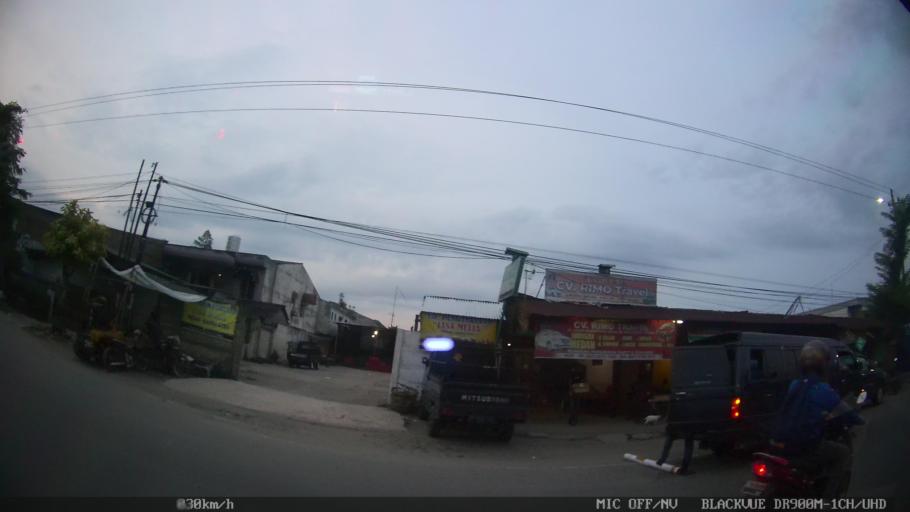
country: ID
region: North Sumatra
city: Sunggal
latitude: 3.5915
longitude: 98.6281
